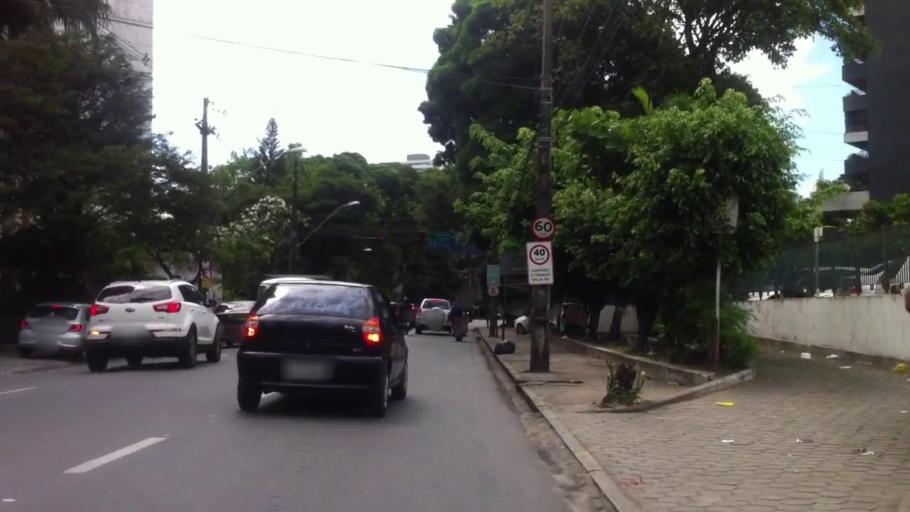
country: BR
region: Pernambuco
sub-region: Recife
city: Recife
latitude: -8.0360
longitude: -34.9071
